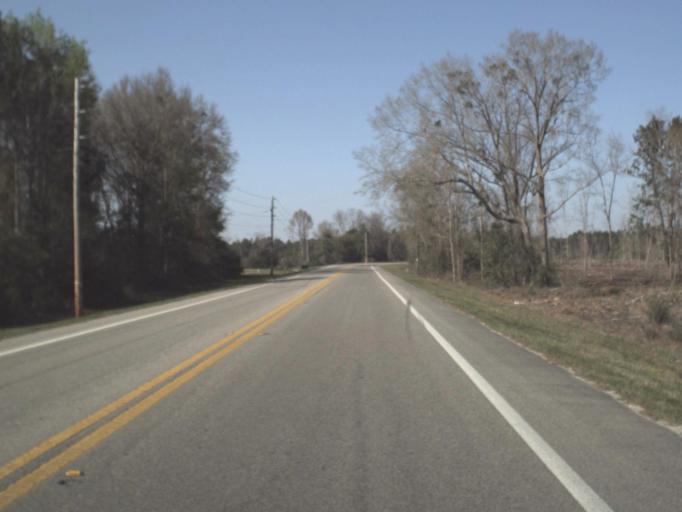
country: US
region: Florida
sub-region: Gulf County
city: Wewahitchka
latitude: 30.1597
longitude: -85.2093
